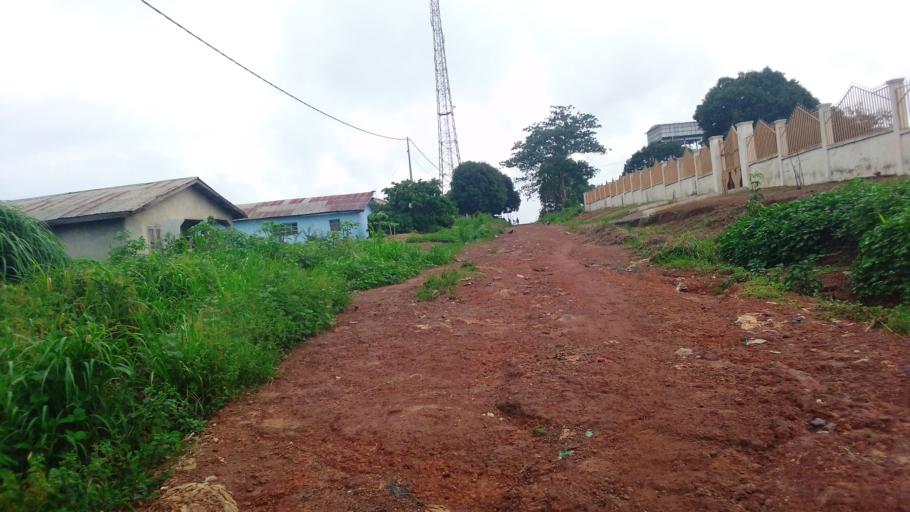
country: SL
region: Northern Province
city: Lunsar
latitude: 8.6855
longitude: -12.5274
